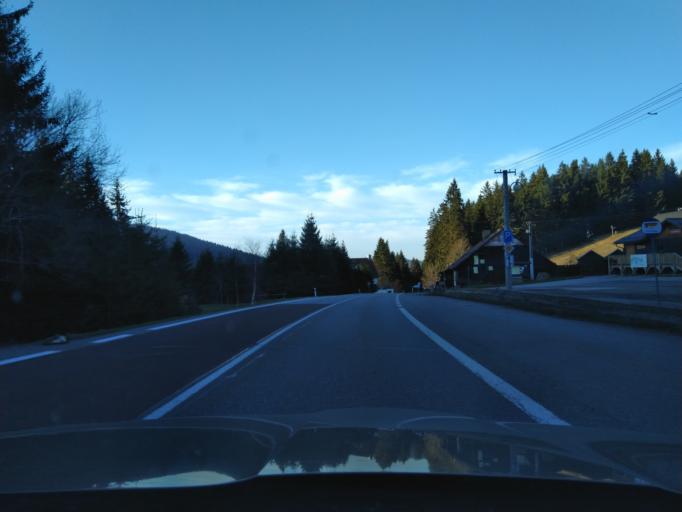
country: CZ
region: Jihocesky
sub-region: Okres Prachatice
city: Vimperk
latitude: 48.9847
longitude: 13.7720
